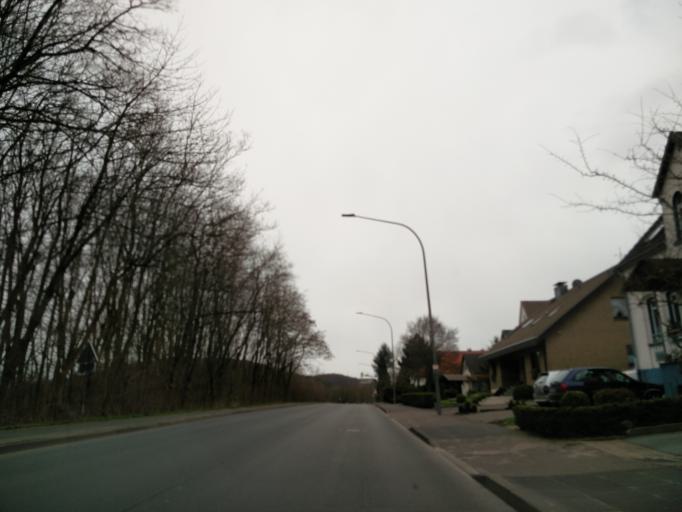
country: DE
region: North Rhine-Westphalia
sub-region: Regierungsbezirk Detmold
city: Horn
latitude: 51.8406
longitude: 8.9727
